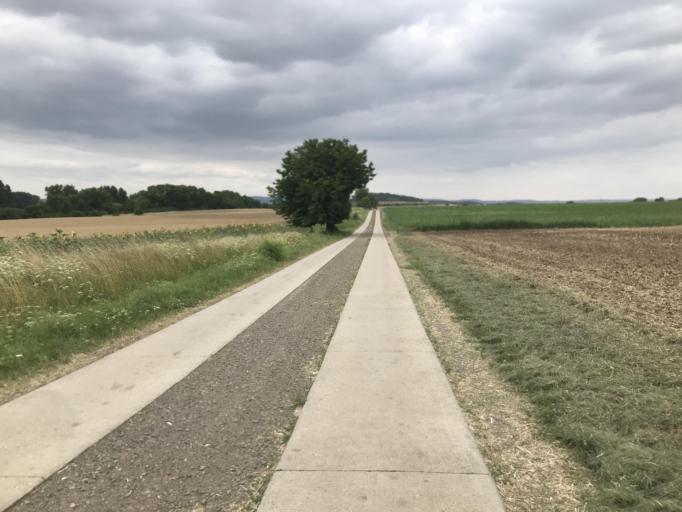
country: DE
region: Saxony-Anhalt
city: Ditfurt
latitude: 51.8224
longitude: 11.1845
